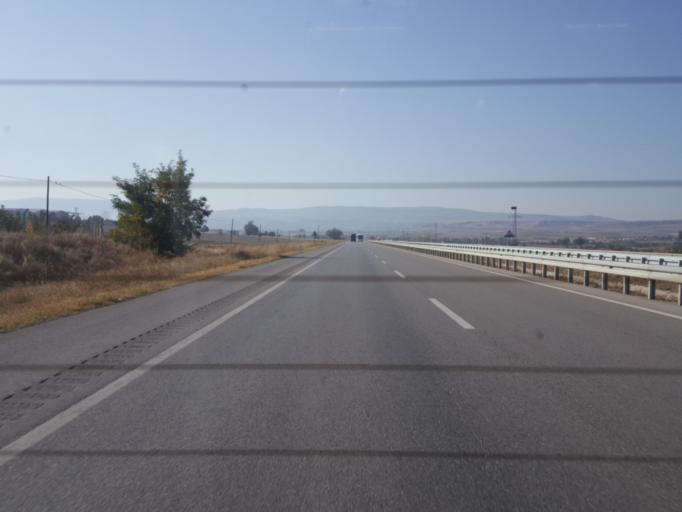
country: TR
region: Amasya
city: Merzifon
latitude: 40.8129
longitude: 35.4575
